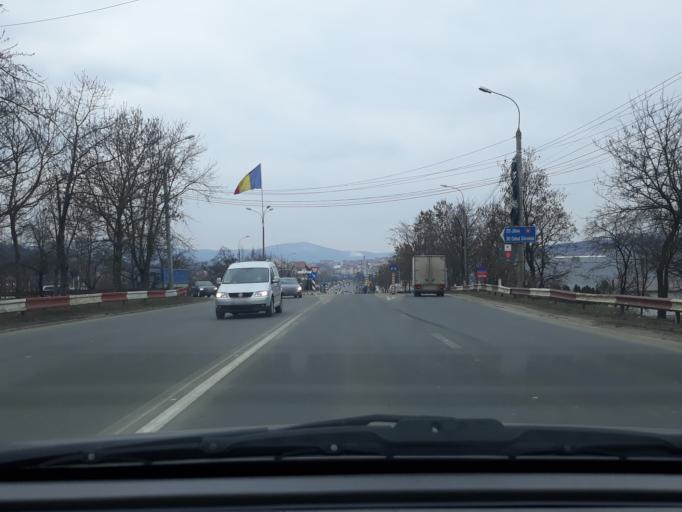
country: RO
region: Salaj
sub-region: Comuna Criseni
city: Criseni
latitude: 47.2174
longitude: 23.0415
